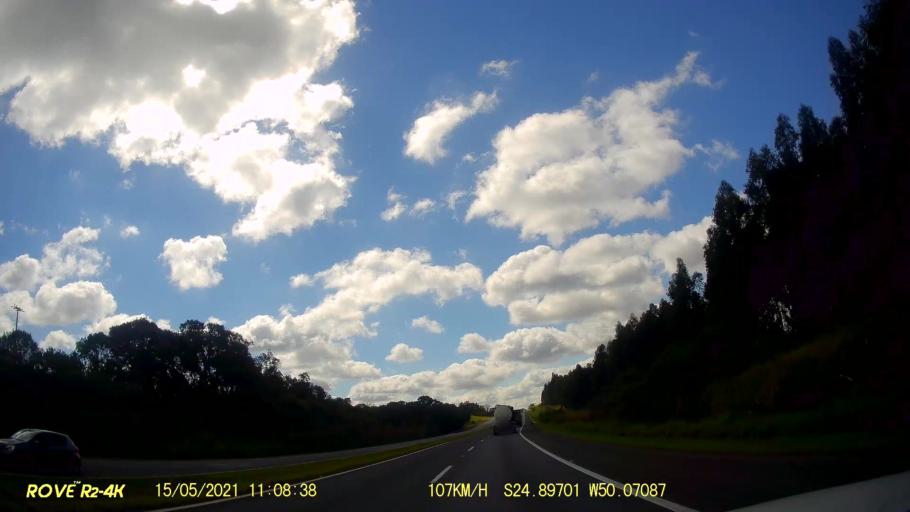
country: BR
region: Parana
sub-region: Carambei
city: Carambei
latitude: -24.8971
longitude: -50.0712
